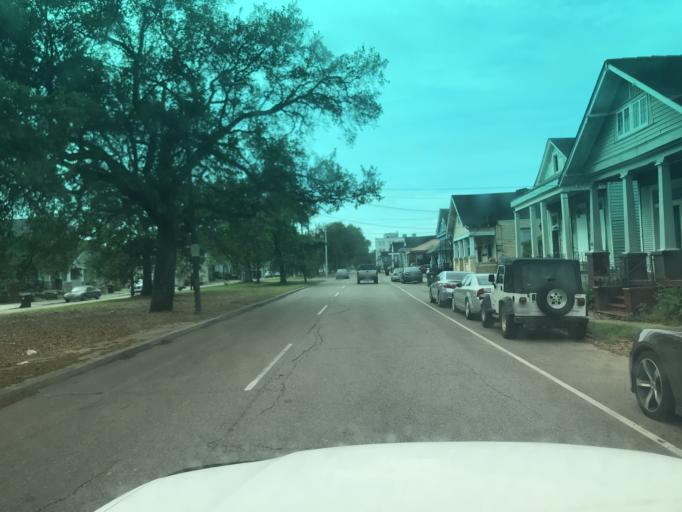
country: US
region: Louisiana
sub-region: Orleans Parish
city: New Orleans
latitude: 29.9790
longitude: -90.0485
